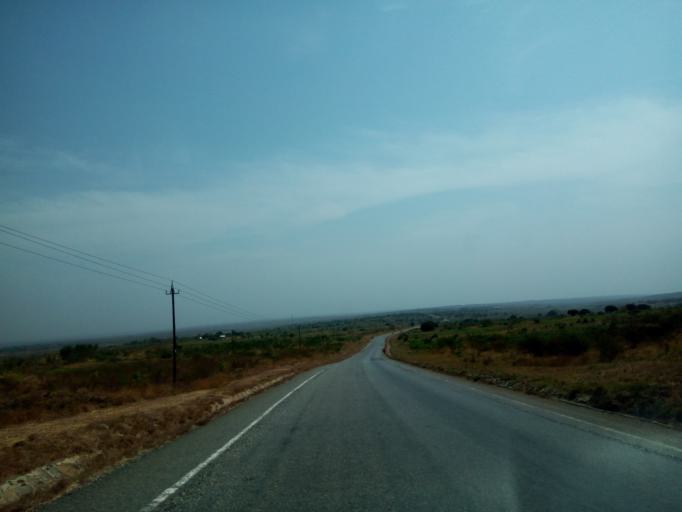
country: UG
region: Northern Region
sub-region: Nebbi District
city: Nebbi
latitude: 2.4627
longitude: 31.2948
